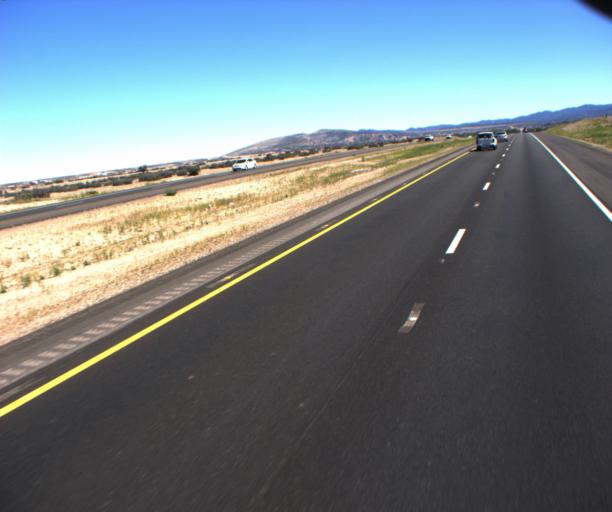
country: US
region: Arizona
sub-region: Yavapai County
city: Chino Valley
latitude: 34.6670
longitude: -112.4392
